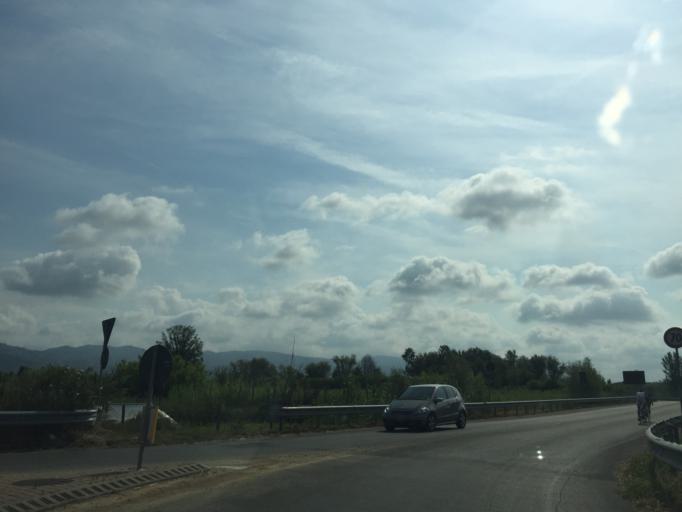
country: IT
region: Tuscany
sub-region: Provincia di Pistoia
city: San Rocco
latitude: 43.8141
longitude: 10.8509
